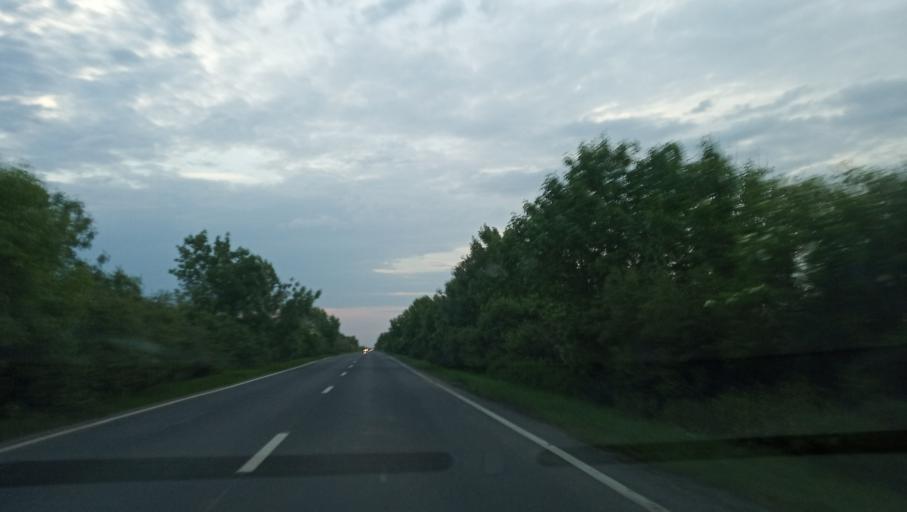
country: RO
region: Timis
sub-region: Comuna Jebel
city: Jebel
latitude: 45.5169
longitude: 21.2346
